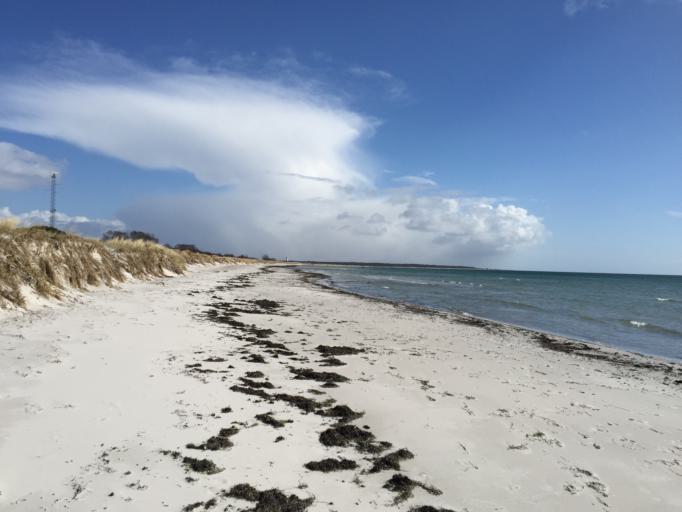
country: SE
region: Skane
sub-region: Vellinge Kommun
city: Skanor med Falsterbo
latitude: 55.3913
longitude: 12.8530
